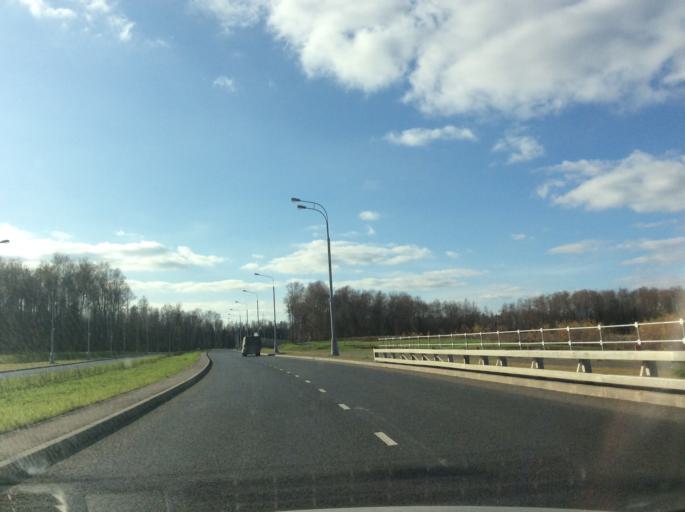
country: RU
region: Moskovskaya
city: Vatutinki
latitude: 55.4878
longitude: 37.3910
